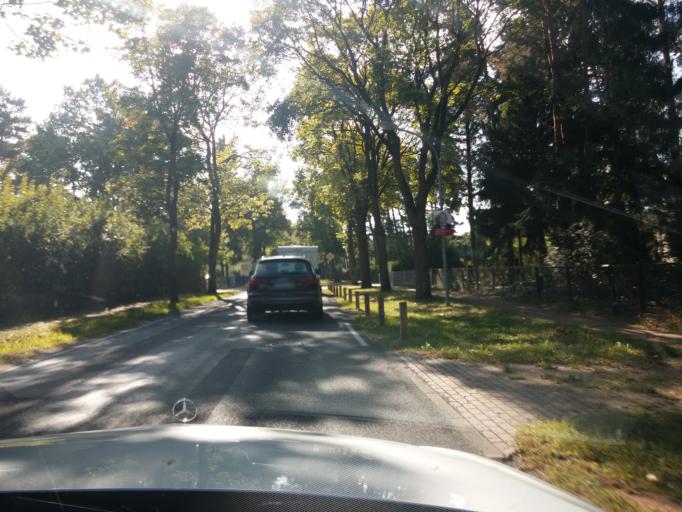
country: DE
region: Brandenburg
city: Fichtenwalde
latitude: 52.2737
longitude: 12.8955
